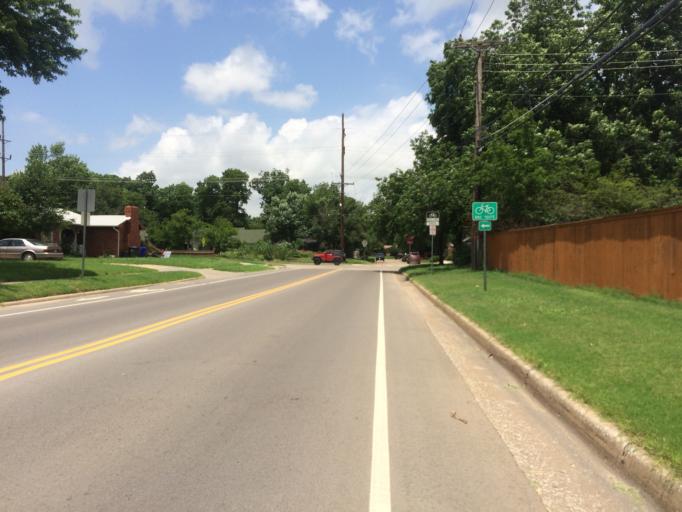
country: US
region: Oklahoma
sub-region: Cleveland County
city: Norman
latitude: 35.2105
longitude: -97.4677
